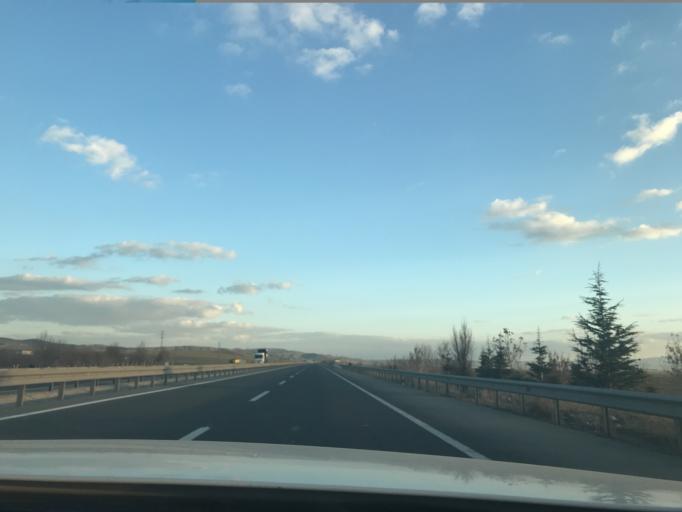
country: TR
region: Ankara
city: Altpinar
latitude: 39.3930
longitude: 32.8830
